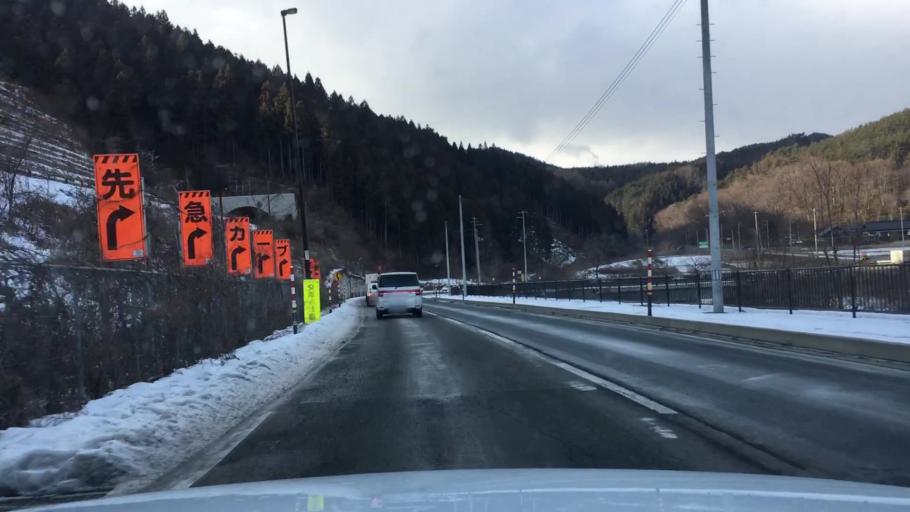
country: JP
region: Iwate
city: Morioka-shi
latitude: 39.6721
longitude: 141.2303
